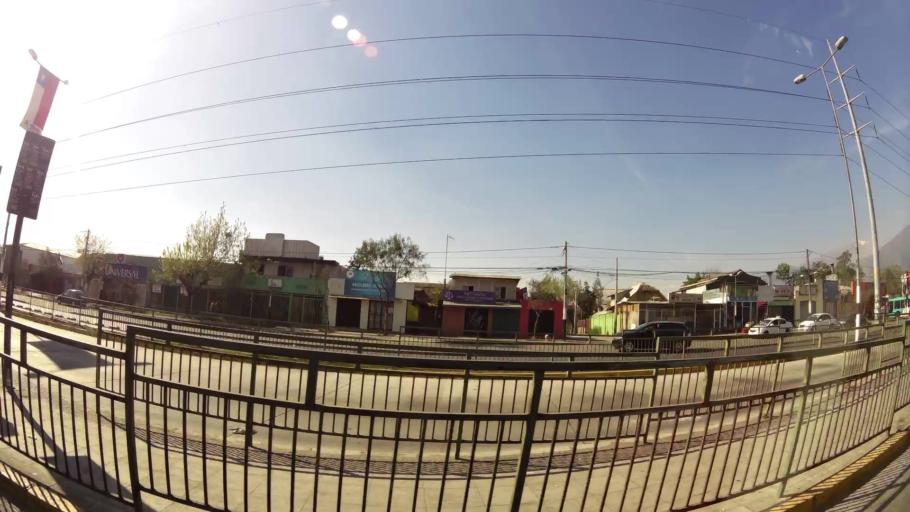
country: CL
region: Santiago Metropolitan
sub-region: Provincia de Santiago
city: Villa Presidente Frei, Nunoa, Santiago, Chile
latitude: -33.4718
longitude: -70.5635
